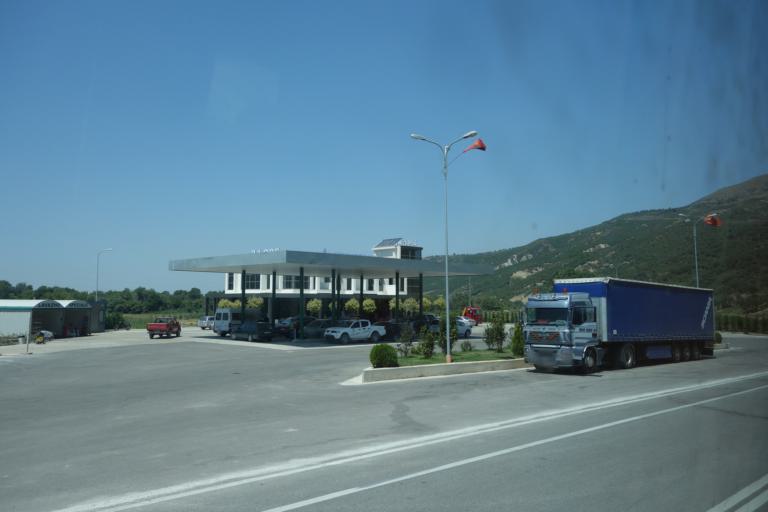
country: AL
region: Fier
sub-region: Rrethi i Mallakastres
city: Hekal
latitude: 40.5179
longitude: 19.7419
